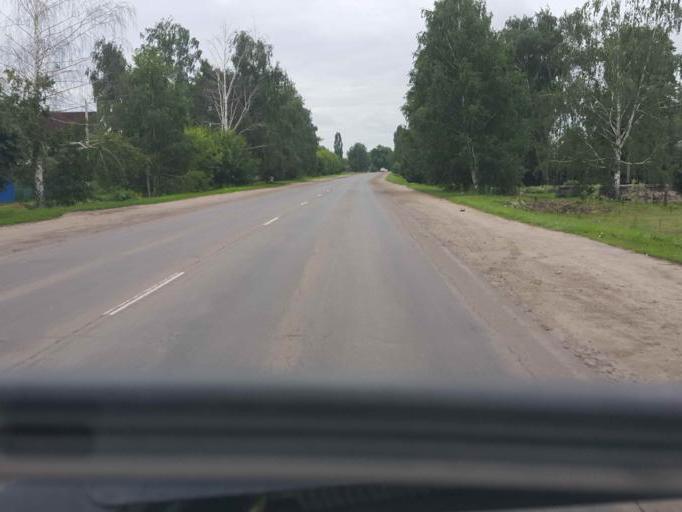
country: RU
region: Tambov
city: Zavoronezhskoye
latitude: 52.8856
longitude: 40.5553
